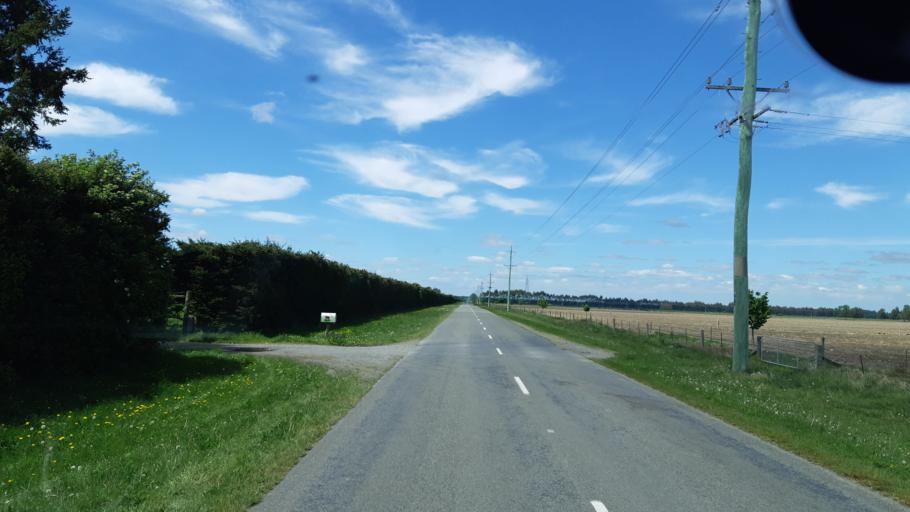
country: NZ
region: Canterbury
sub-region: Ashburton District
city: Methven
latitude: -43.7226
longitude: 171.4773
